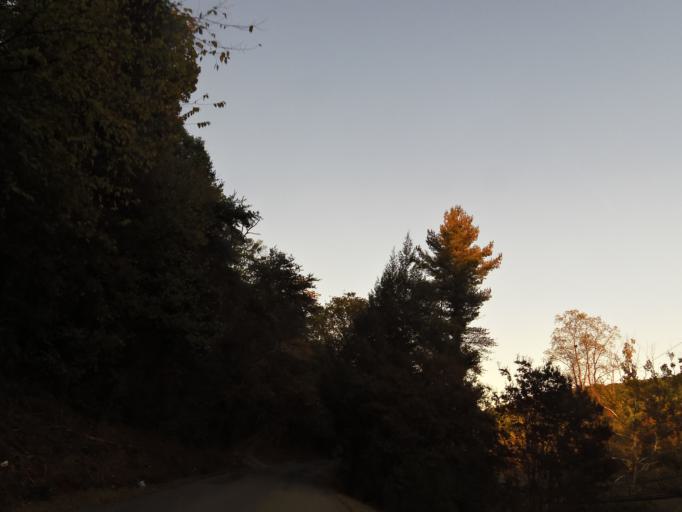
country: US
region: Tennessee
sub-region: Blount County
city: Eagleton Village
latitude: 35.8356
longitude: -83.9264
